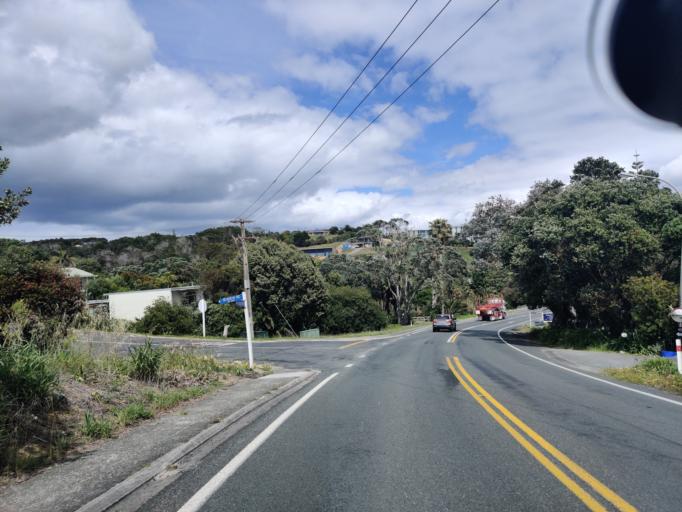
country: NZ
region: Northland
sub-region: Far North District
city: Taipa
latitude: -34.9914
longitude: 173.4863
